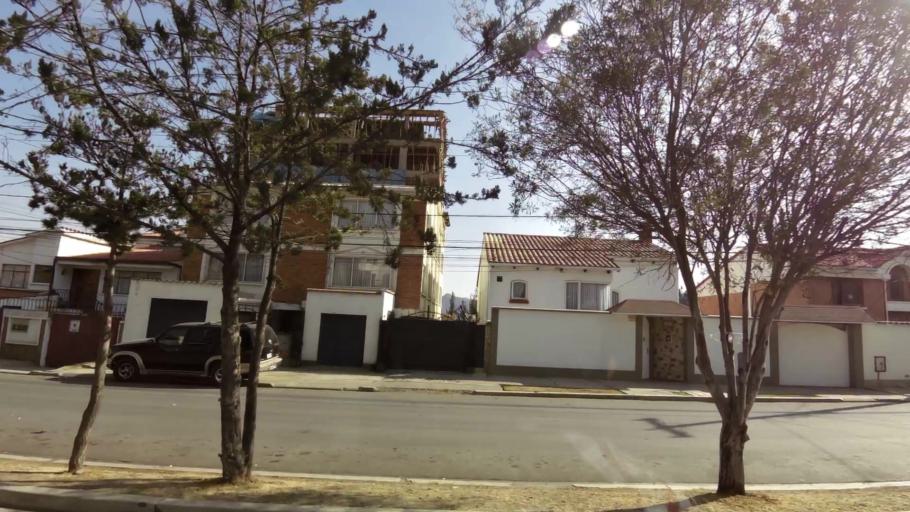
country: BO
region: La Paz
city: La Paz
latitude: -16.5278
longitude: -68.0716
